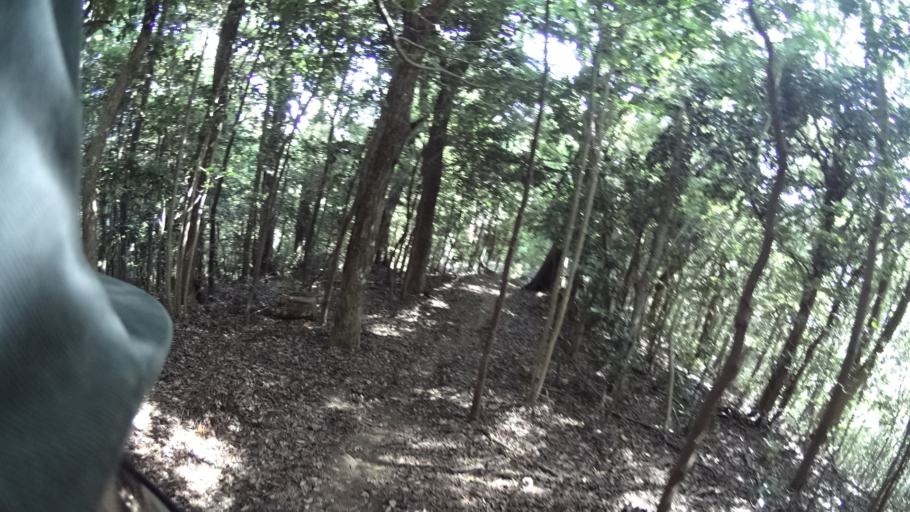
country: JP
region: Shizuoka
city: Kosai-shi
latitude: 34.7837
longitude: 137.4964
